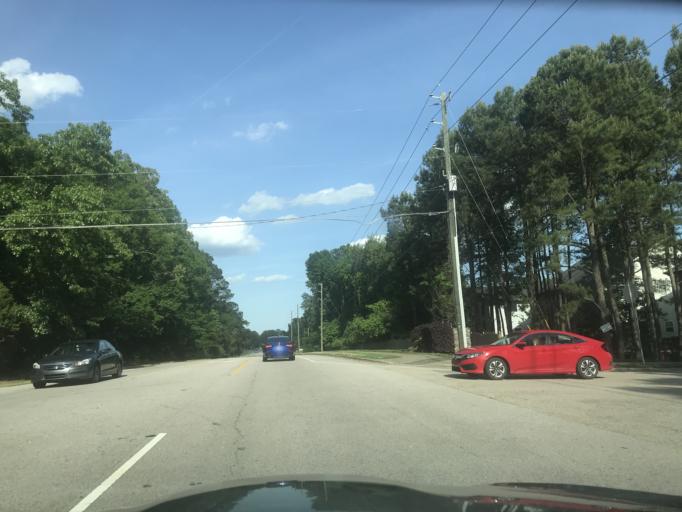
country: US
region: North Carolina
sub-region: Wake County
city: Knightdale
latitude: 35.8560
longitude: -78.5626
